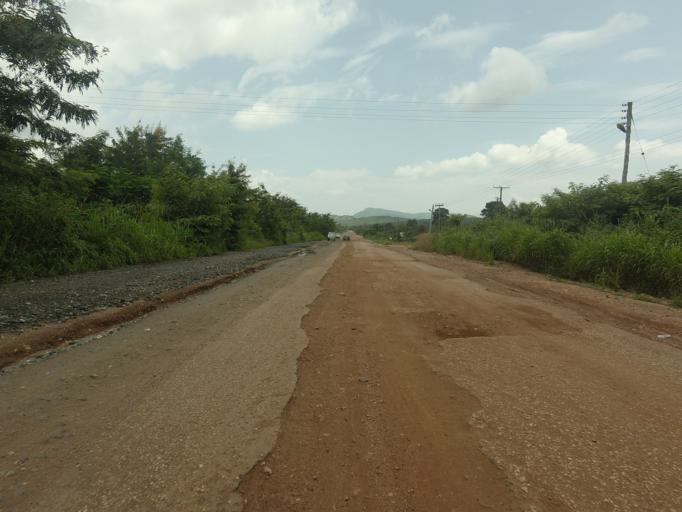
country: GH
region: Volta
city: Ho
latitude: 6.6803
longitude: 0.3254
